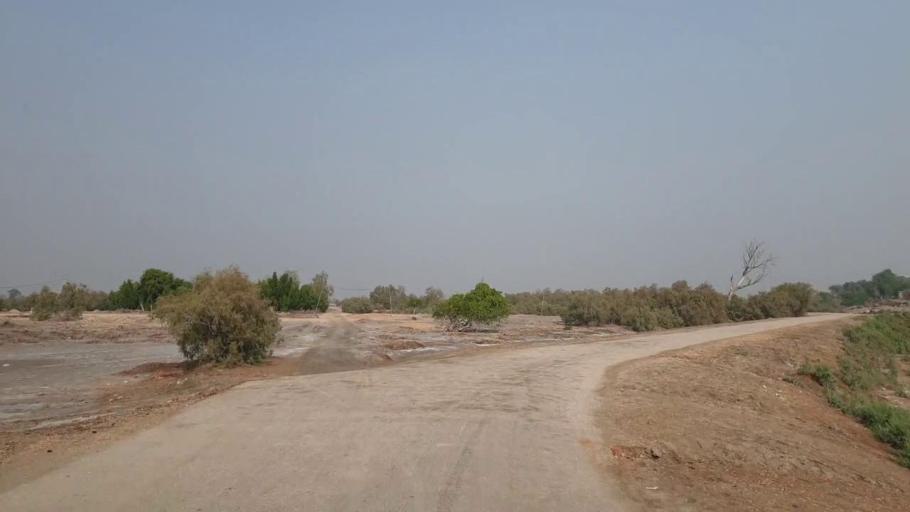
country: PK
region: Sindh
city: Bhan
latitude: 26.4885
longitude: 67.7001
